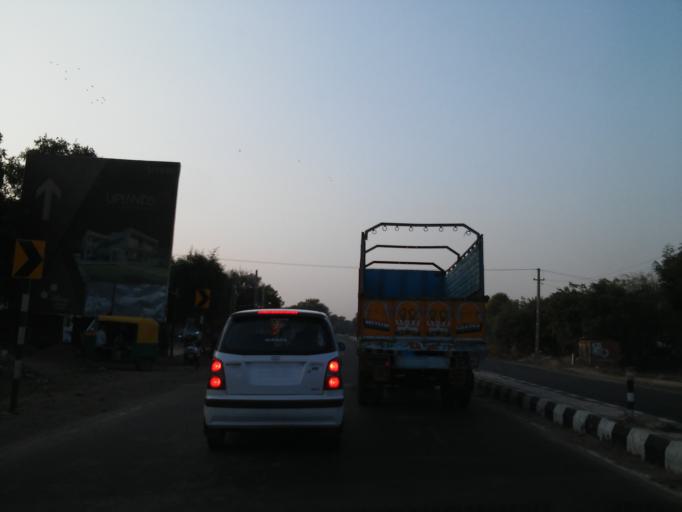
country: IN
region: Gujarat
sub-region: Ahmadabad
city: Sanand
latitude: 23.0655
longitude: 72.4429
